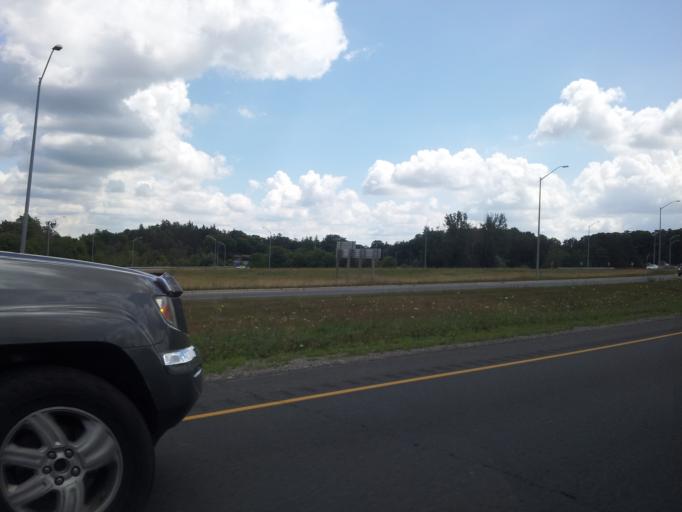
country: CA
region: Ontario
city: Waterloo
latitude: 43.4762
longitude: -80.4963
